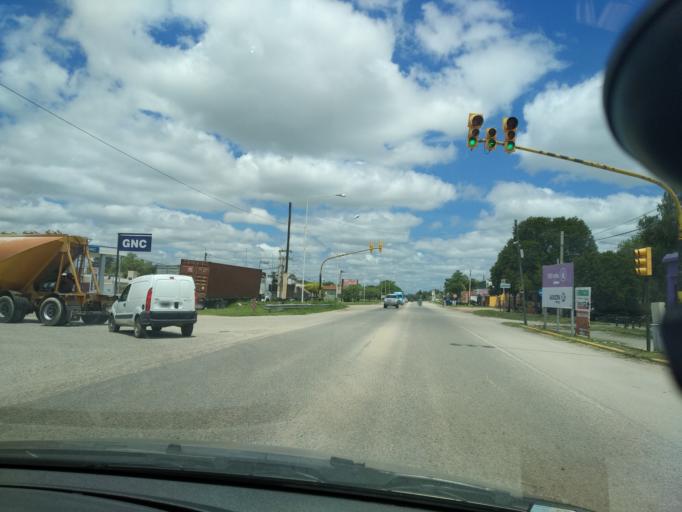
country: AR
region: Cordoba
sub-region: Departamento de Rio Segundo
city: Rio Segundo
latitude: -31.6471
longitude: -63.9053
